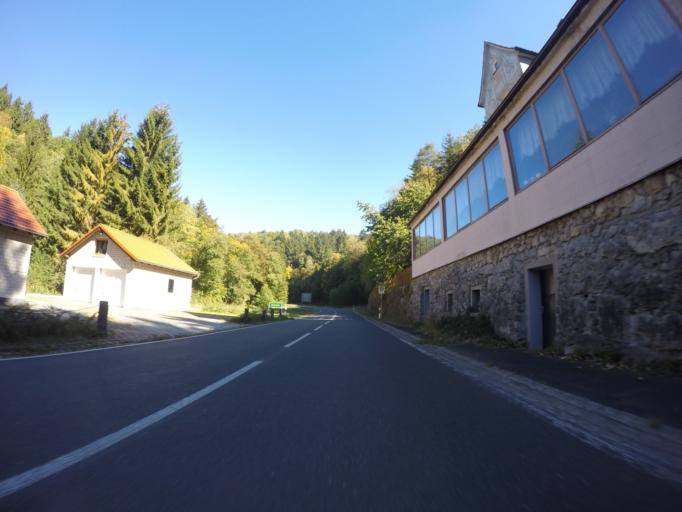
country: DE
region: Bavaria
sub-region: Upper Franconia
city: Waischenfeld
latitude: 49.8104
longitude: 11.3641
